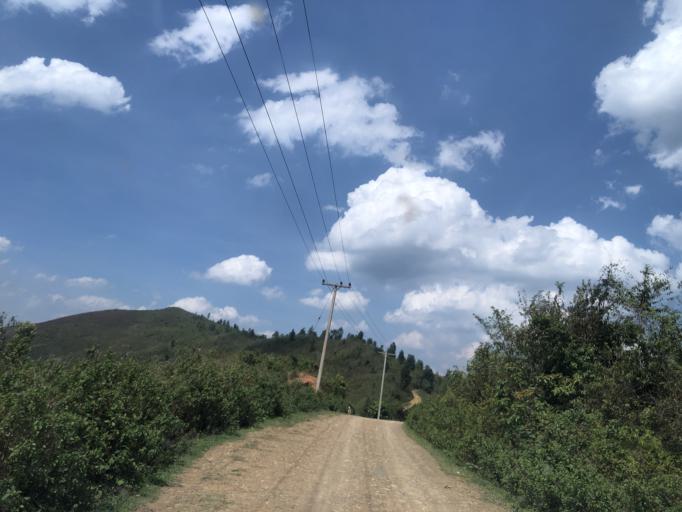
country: LA
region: Phongsali
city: Phongsali
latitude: 21.4028
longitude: 102.2285
